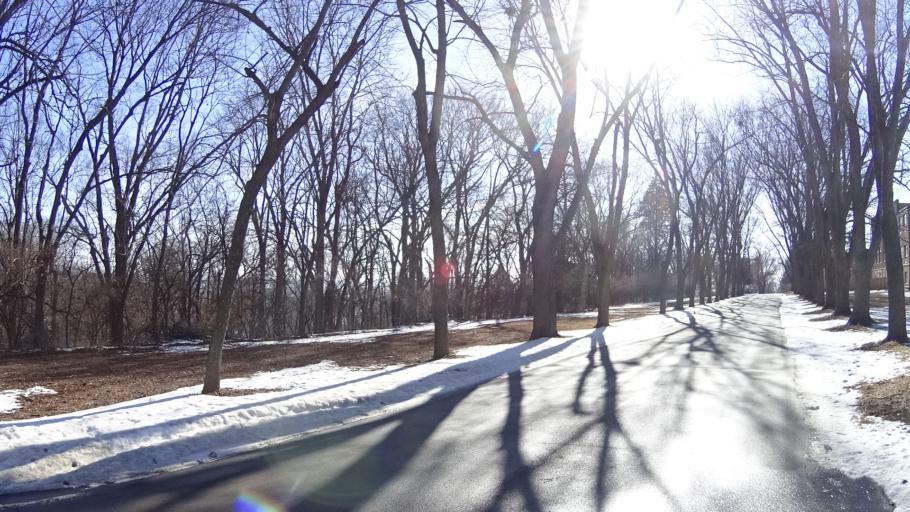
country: US
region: Nebraska
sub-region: Sarpy County
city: Bellevue
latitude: 41.1417
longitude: -95.9034
